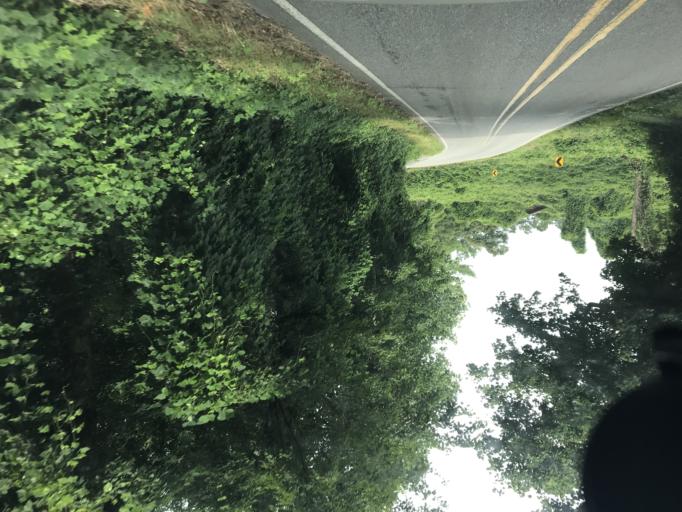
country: US
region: Georgia
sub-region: Cherokee County
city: Ball Ground
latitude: 34.3301
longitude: -84.2619
